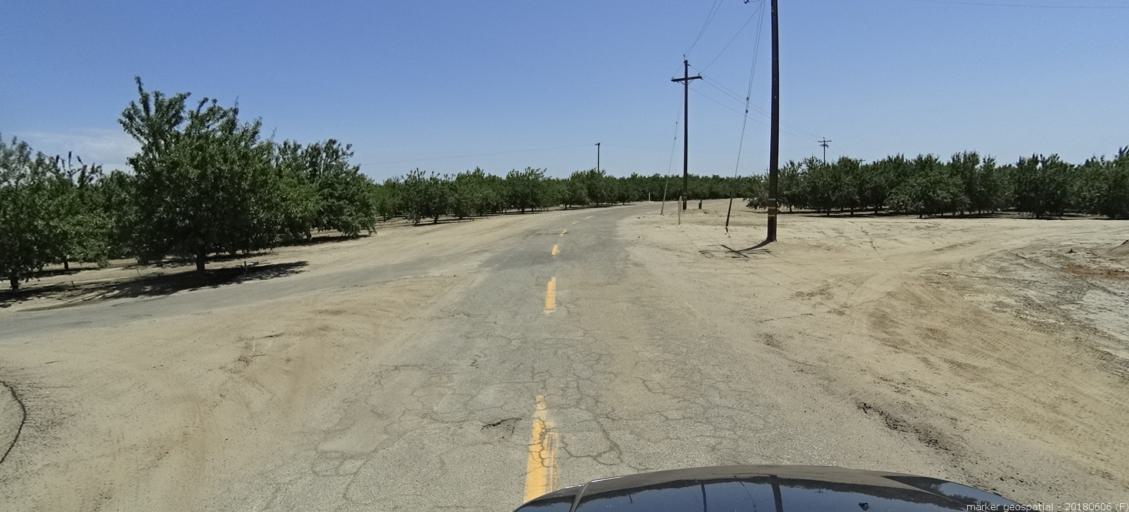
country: US
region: California
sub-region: Fresno County
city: Mendota
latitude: 36.8047
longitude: -120.3411
